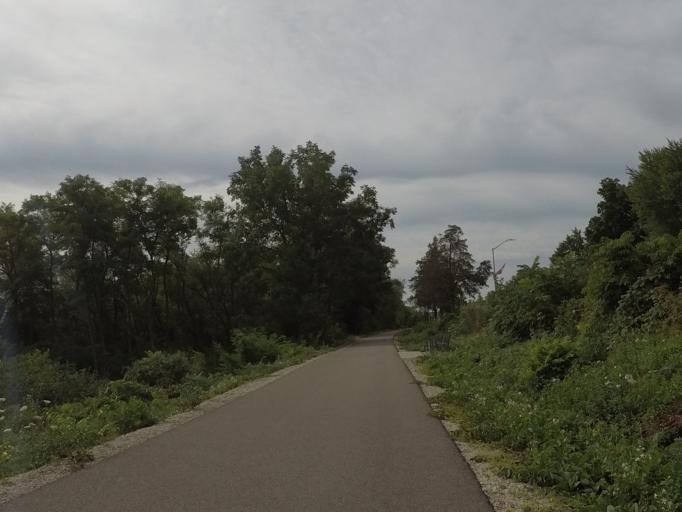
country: US
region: Wisconsin
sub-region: Sauk County
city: Prairie du Sac
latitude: 43.2854
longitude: -89.7178
